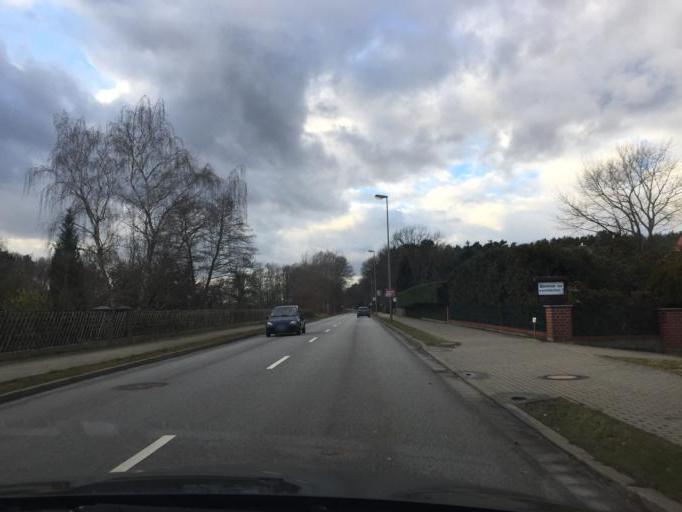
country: DE
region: Brandenburg
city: Kolkwitz
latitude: 51.7501
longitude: 14.2364
